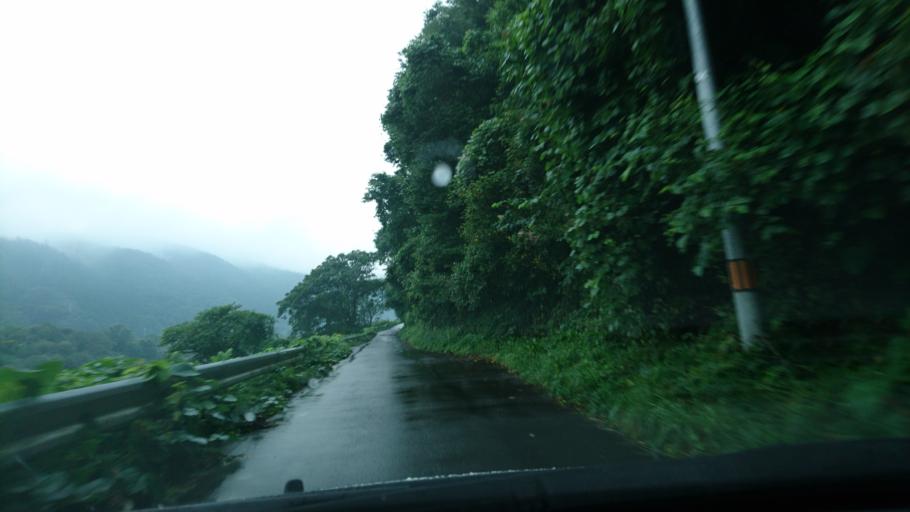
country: JP
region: Iwate
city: Ichinoseki
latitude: 38.8741
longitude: 141.2600
